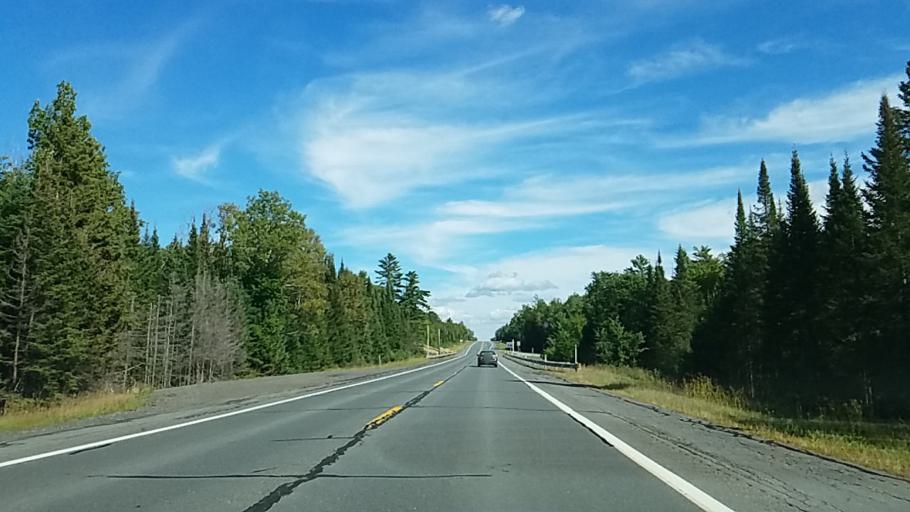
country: US
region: Michigan
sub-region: Baraga County
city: L'Anse
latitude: 46.5757
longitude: -88.3429
